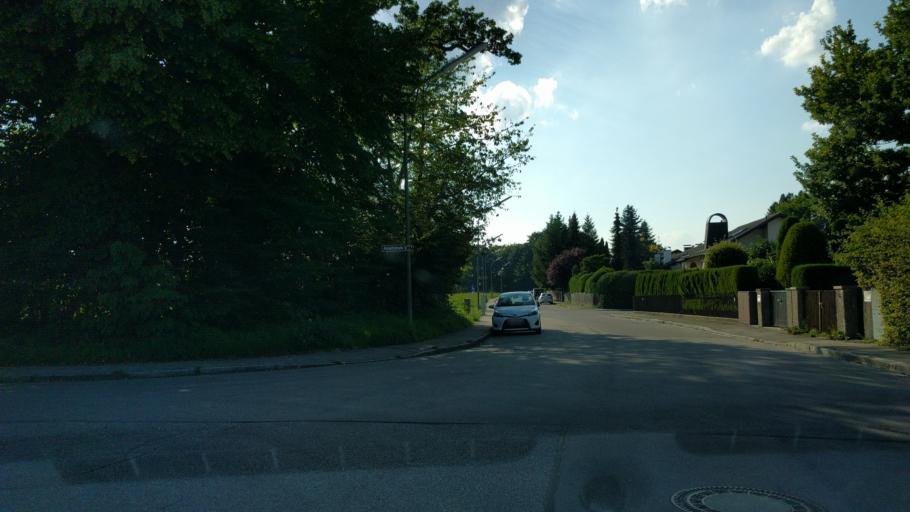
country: DE
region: Bavaria
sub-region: Upper Bavaria
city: Grunwald
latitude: 48.0336
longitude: 11.5189
